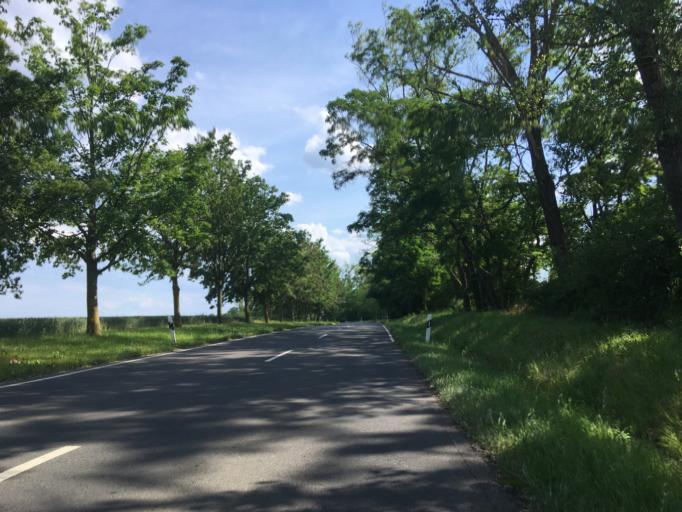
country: DE
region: Brandenburg
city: Steinhofel
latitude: 52.4339
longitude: 14.1012
